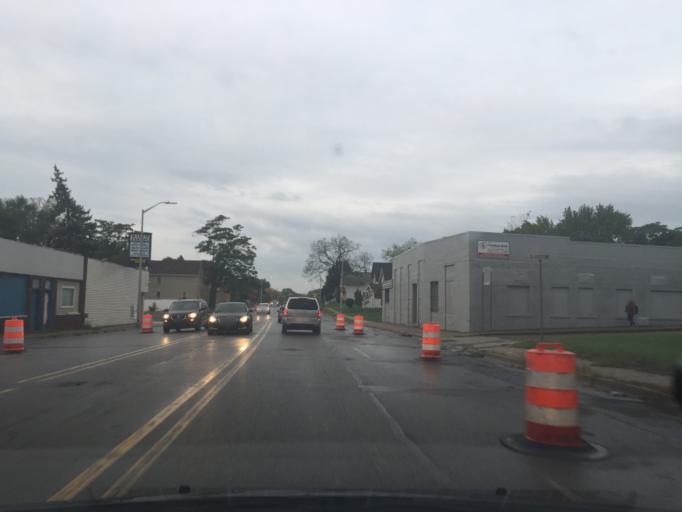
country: US
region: Michigan
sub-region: Oakland County
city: Pontiac
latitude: 42.6459
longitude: -83.2890
